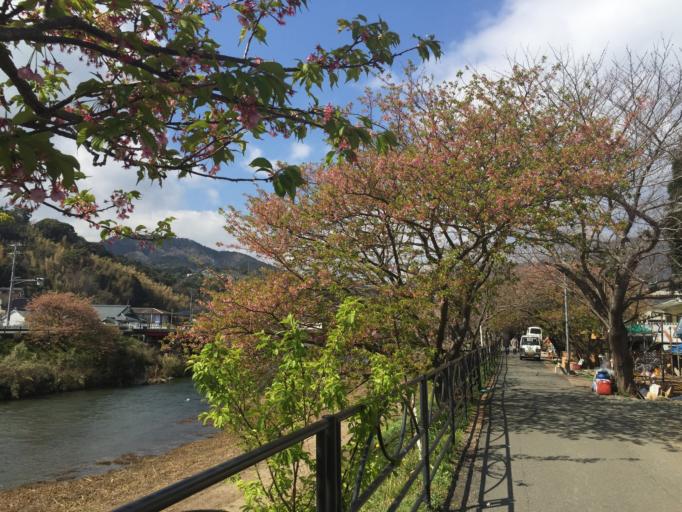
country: JP
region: Shizuoka
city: Shimoda
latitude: 34.7518
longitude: 138.9884
